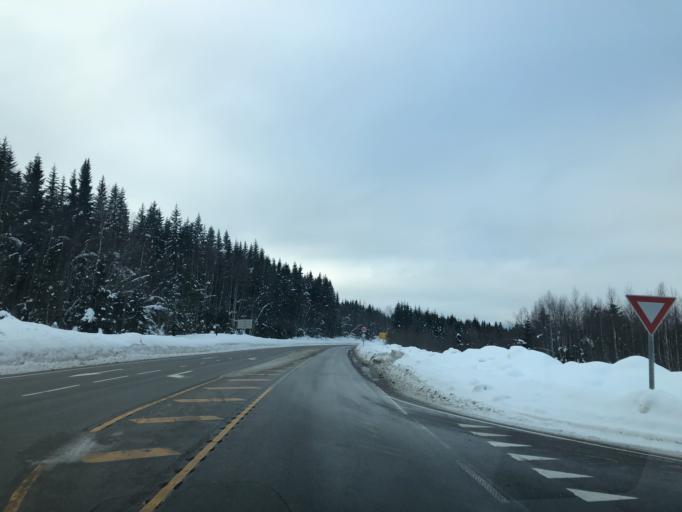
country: NO
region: Hedmark
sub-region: Trysil
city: Innbygda
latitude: 61.2711
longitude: 12.2987
